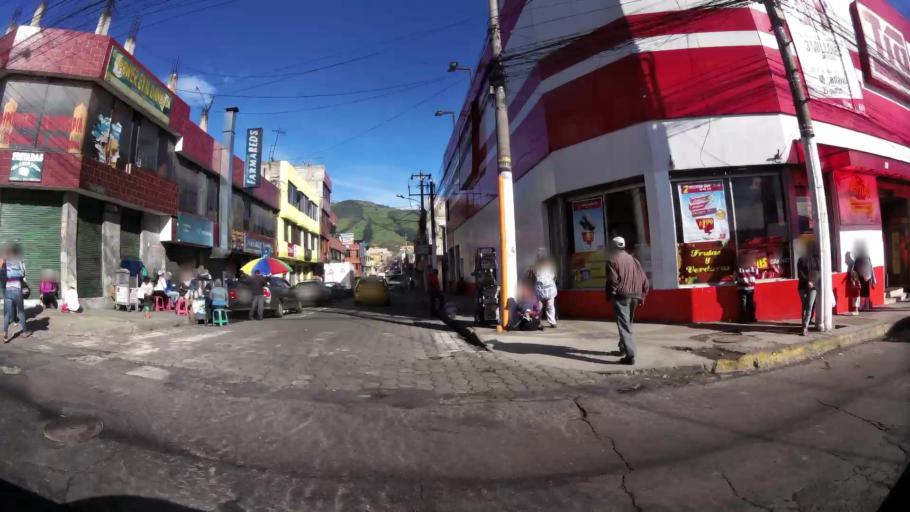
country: EC
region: Pichincha
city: Quito
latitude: -0.3186
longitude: -78.5495
